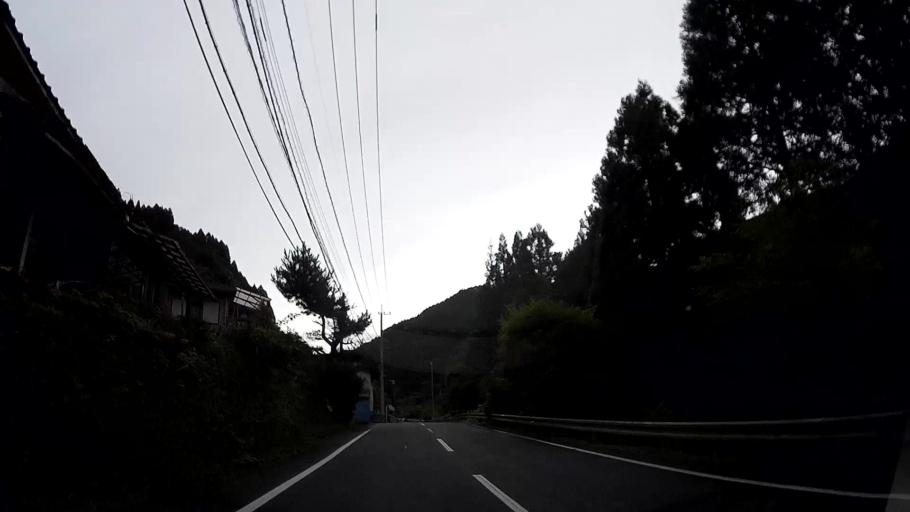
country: JP
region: Kumamoto
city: Kikuchi
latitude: 33.0863
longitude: 130.9503
